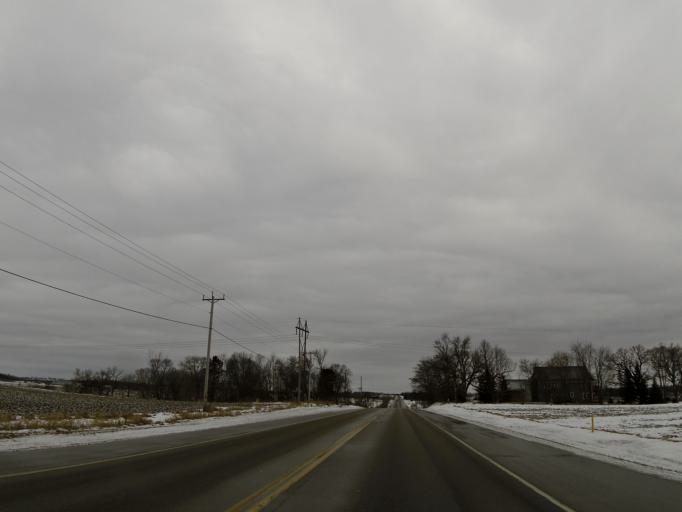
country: US
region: Minnesota
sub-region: Washington County
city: Woodbury
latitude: 44.8848
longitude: -92.9033
